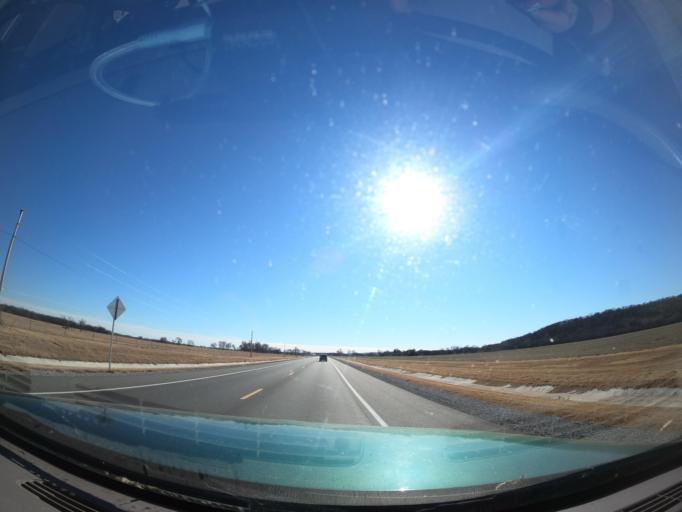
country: US
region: Oklahoma
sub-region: Wagoner County
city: Coweta
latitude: 35.8995
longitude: -95.6592
